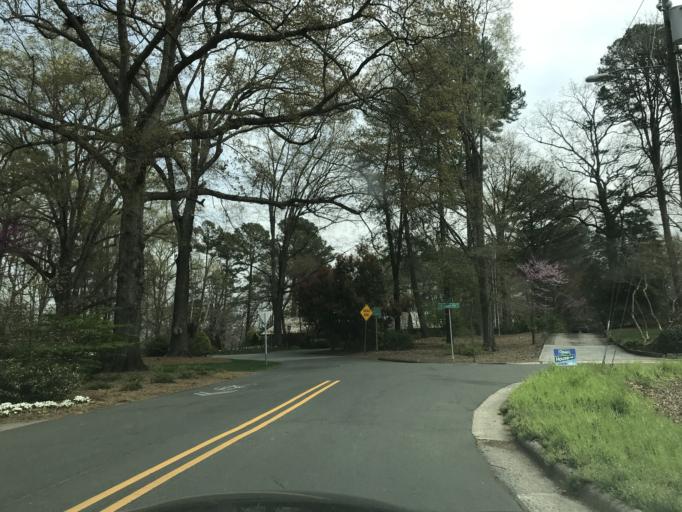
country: US
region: North Carolina
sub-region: Orange County
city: Chapel Hill
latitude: 35.9037
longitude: -79.0360
